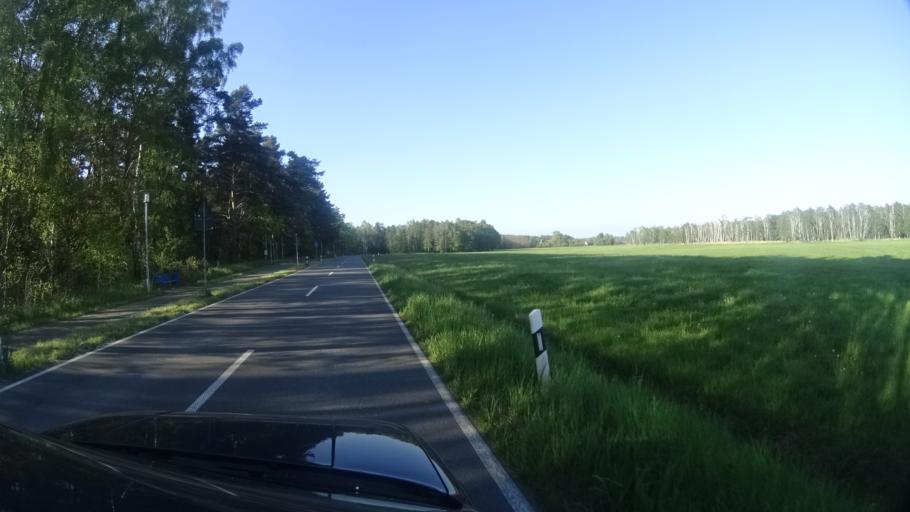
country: DE
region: Mecklenburg-Vorpommern
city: Ostseebad Dierhagen
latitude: 54.2823
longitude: 12.3226
